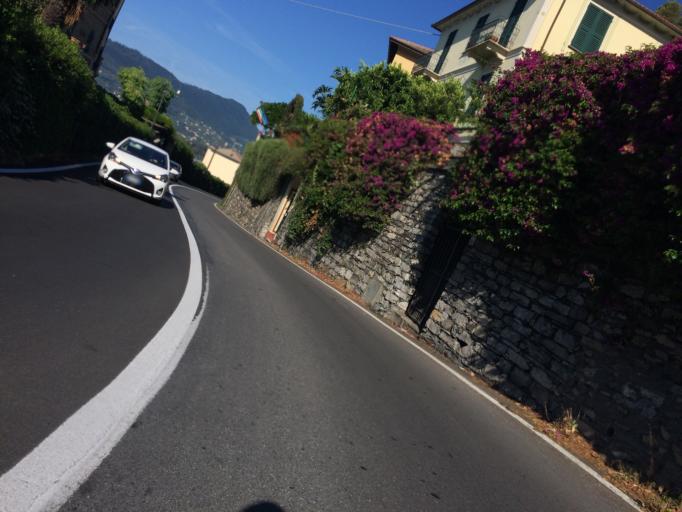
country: IT
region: Liguria
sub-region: Provincia di Genova
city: Zoagli
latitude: 44.3411
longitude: 9.2503
